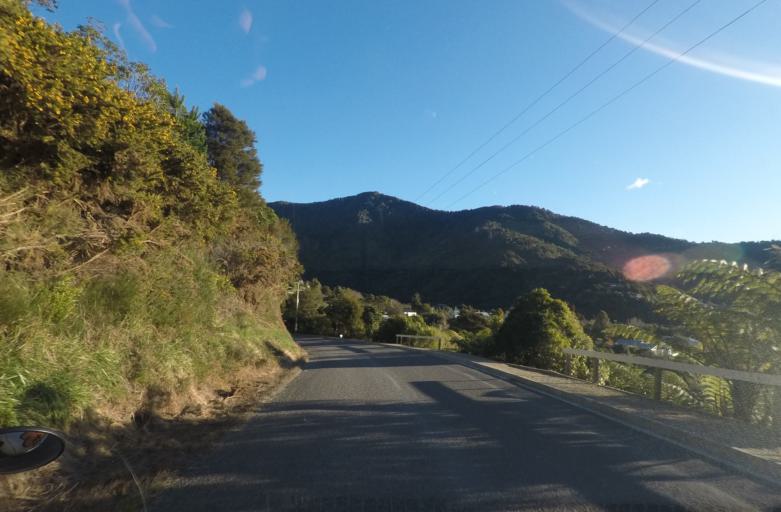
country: NZ
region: Marlborough
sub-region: Marlborough District
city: Picton
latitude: -41.2743
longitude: 173.9670
